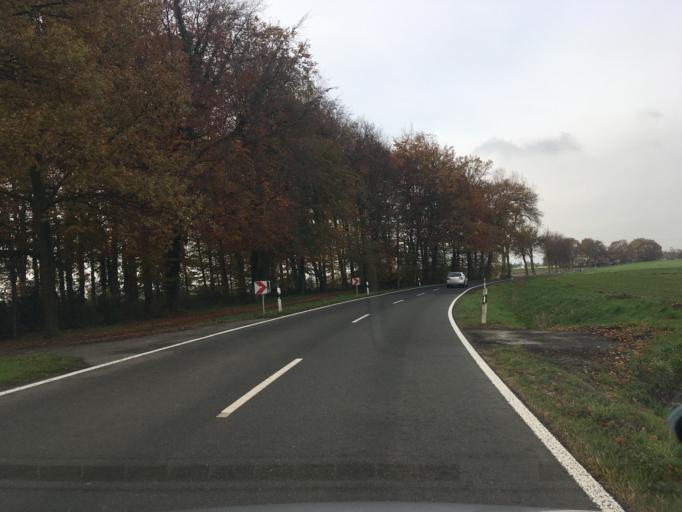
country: DE
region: North Rhine-Westphalia
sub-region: Regierungsbezirk Munster
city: Velen
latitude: 51.9128
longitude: 6.9658
